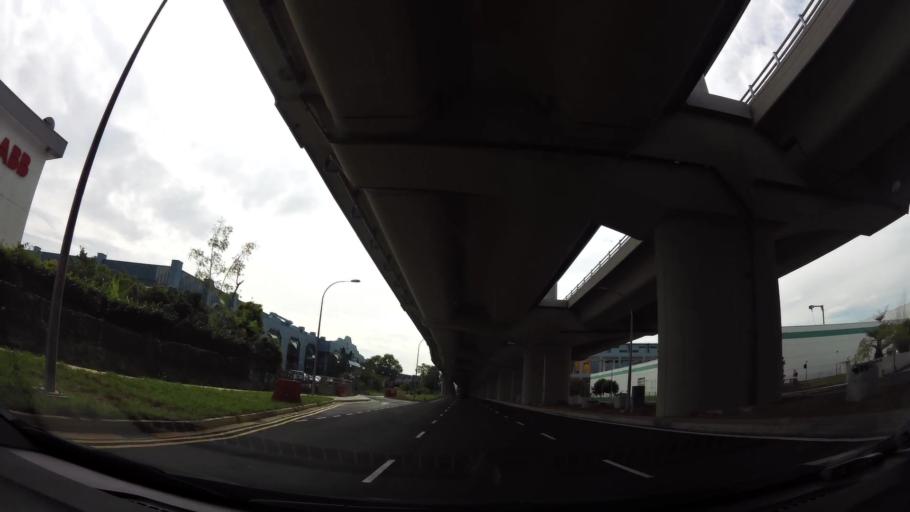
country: MY
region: Johor
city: Johor Bahru
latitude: 1.3276
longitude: 103.6424
